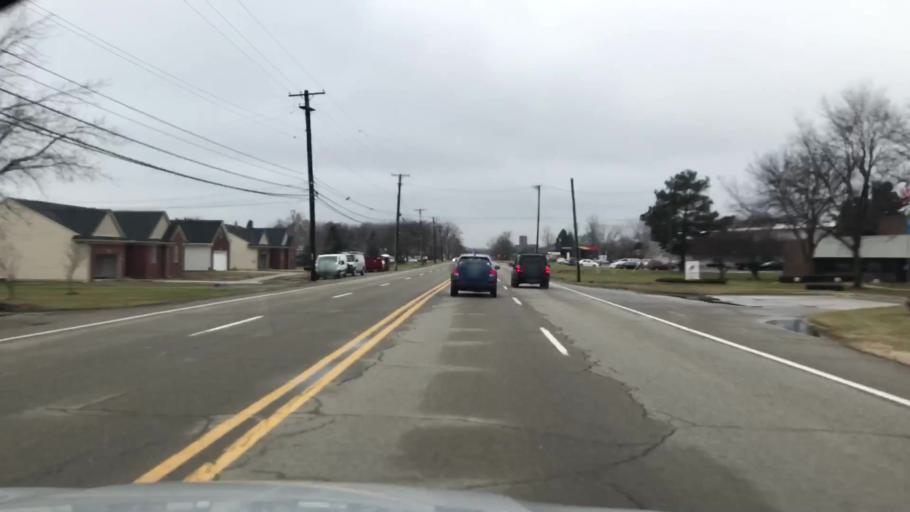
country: US
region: Michigan
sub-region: Wayne County
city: Plymouth
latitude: 42.3711
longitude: -83.4265
